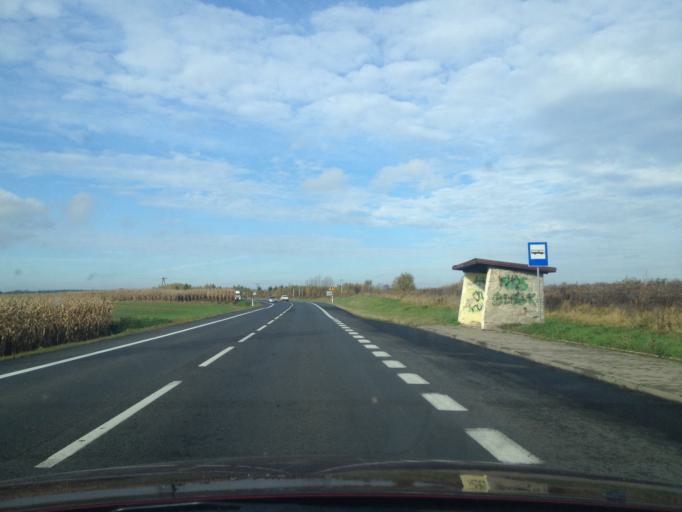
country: PL
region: Lower Silesian Voivodeship
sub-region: Powiat lubanski
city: Pisarzowice
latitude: 51.1397
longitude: 15.2340
